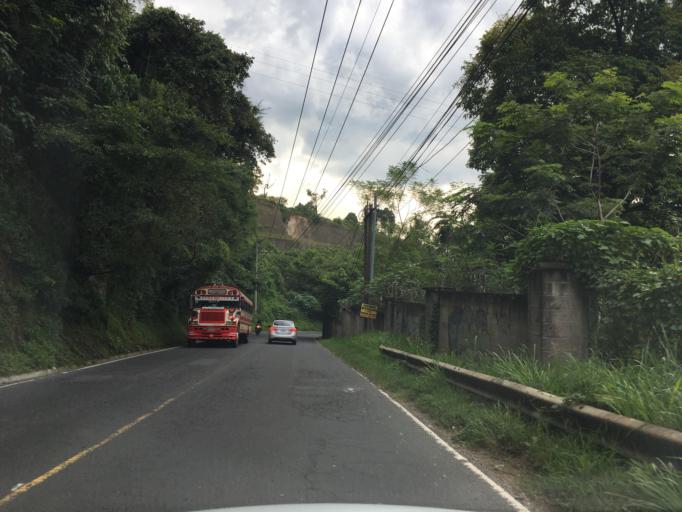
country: GT
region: Guatemala
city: Petapa
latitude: 14.5036
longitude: -90.5395
